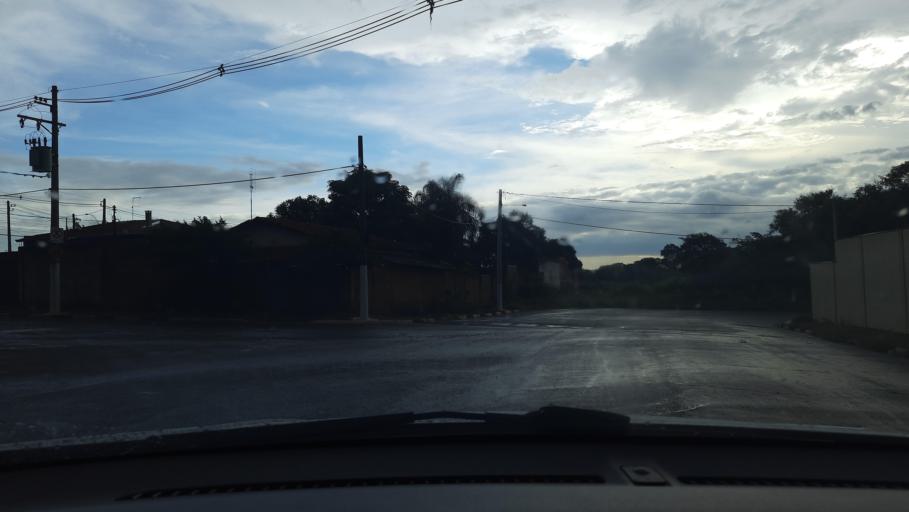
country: BR
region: Sao Paulo
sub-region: Casa Branca
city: Casa Branca
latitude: -21.7566
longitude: -47.0763
